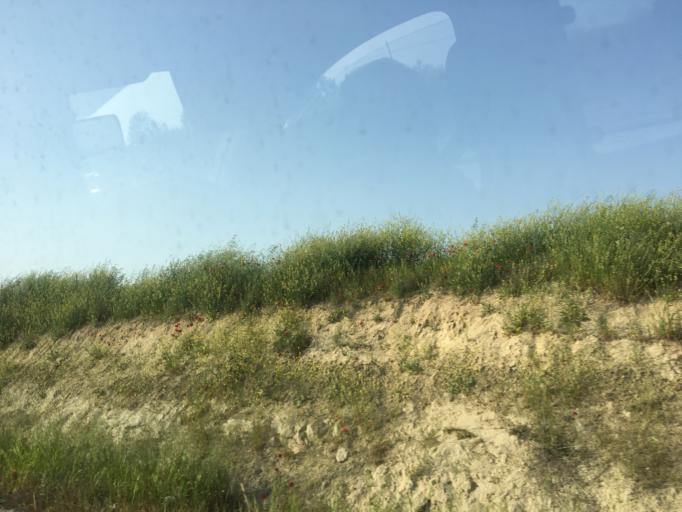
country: TR
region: Manisa
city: Ahmetli
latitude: 38.5662
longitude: 28.0354
